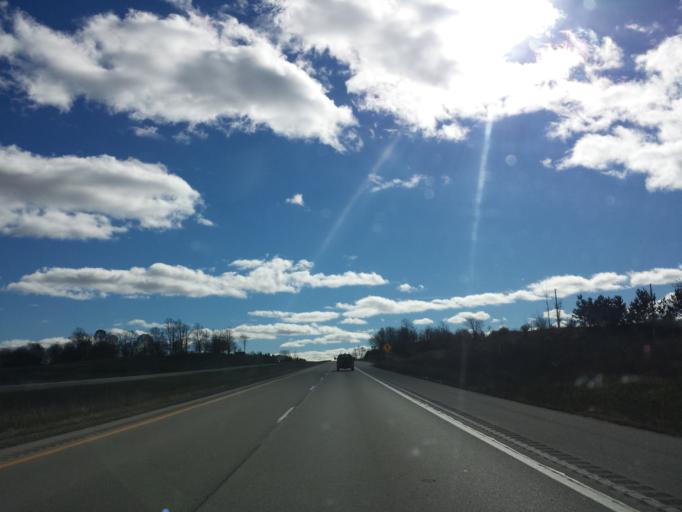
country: US
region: Michigan
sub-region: Cheboygan County
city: Cheboygan
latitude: 45.6358
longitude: -84.6349
